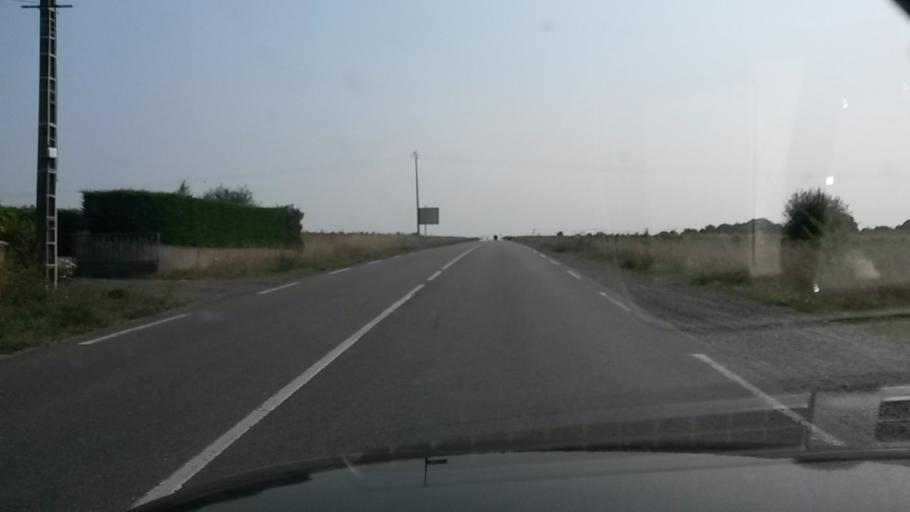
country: FR
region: Pays de la Loire
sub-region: Departement de la Loire-Atlantique
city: Mouzillon
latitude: 47.1347
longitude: -1.2825
